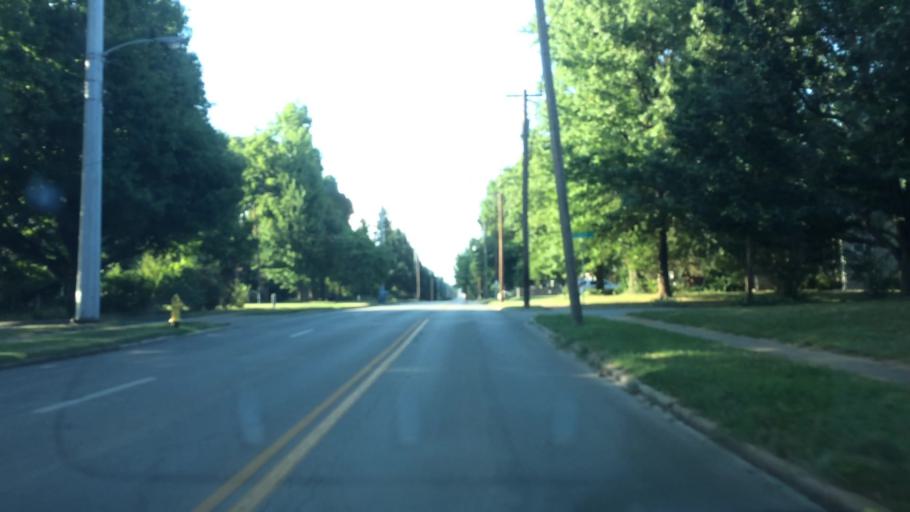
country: US
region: Missouri
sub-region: Greene County
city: Springfield
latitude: 37.1910
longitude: -93.2903
